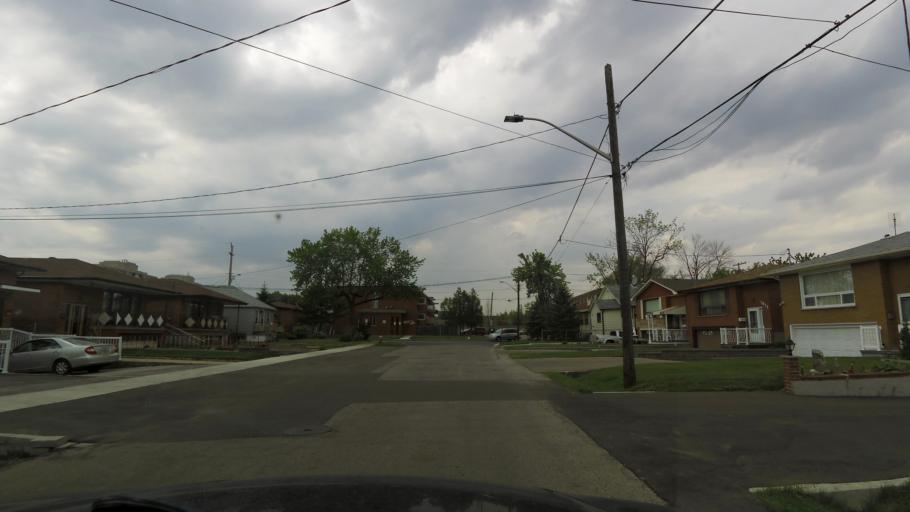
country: CA
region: Ontario
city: Etobicoke
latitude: 43.5737
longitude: -79.5654
